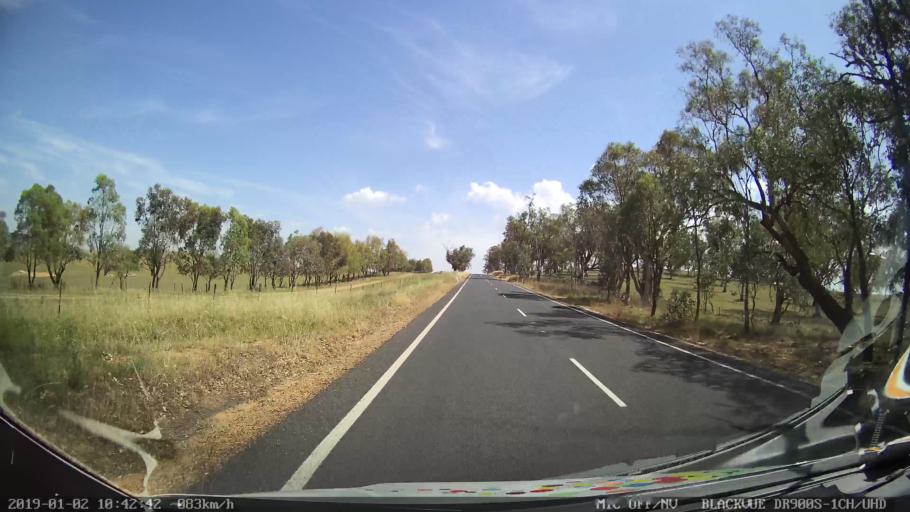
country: AU
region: New South Wales
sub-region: Cootamundra
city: Cootamundra
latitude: -34.7812
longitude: 148.3066
